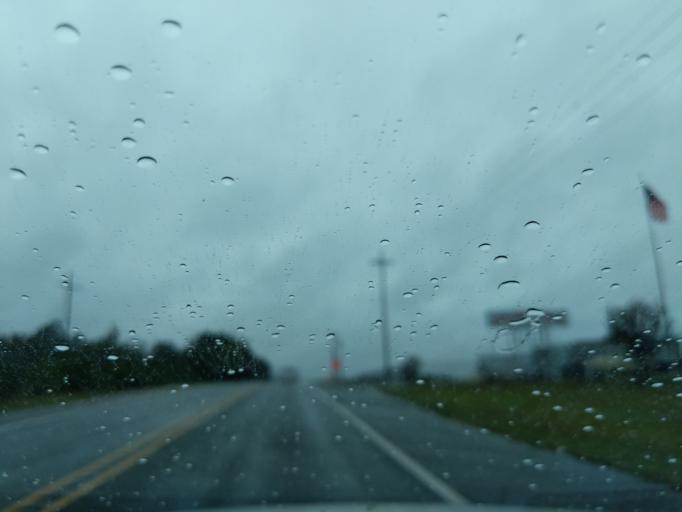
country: US
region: Louisiana
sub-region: Webster Parish
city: Minden
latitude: 32.6055
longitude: -93.2498
